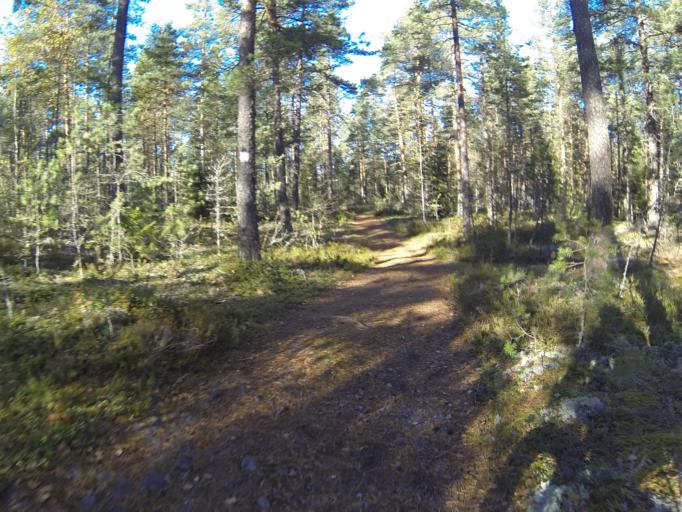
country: FI
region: Varsinais-Suomi
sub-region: Salo
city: Saerkisalo
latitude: 60.1984
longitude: 22.9263
